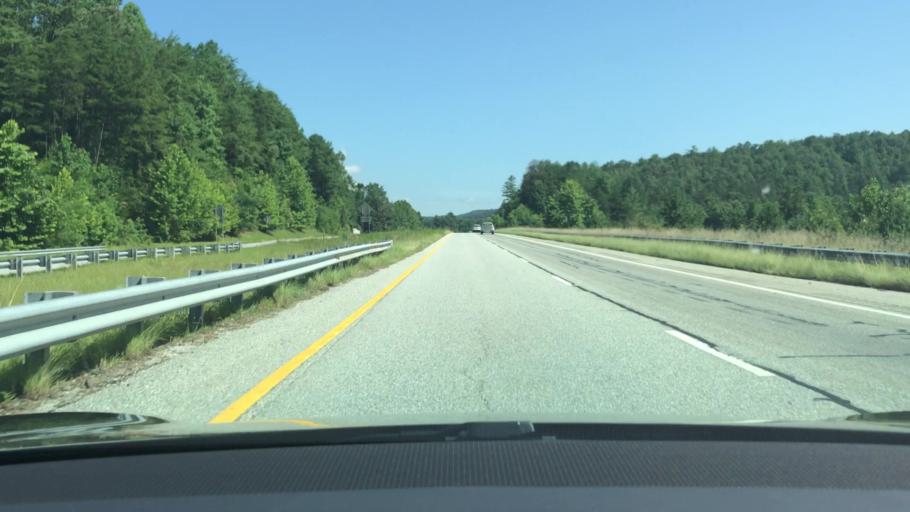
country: US
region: Georgia
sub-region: Rabun County
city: Clayton
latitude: 34.7614
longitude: -83.3968
